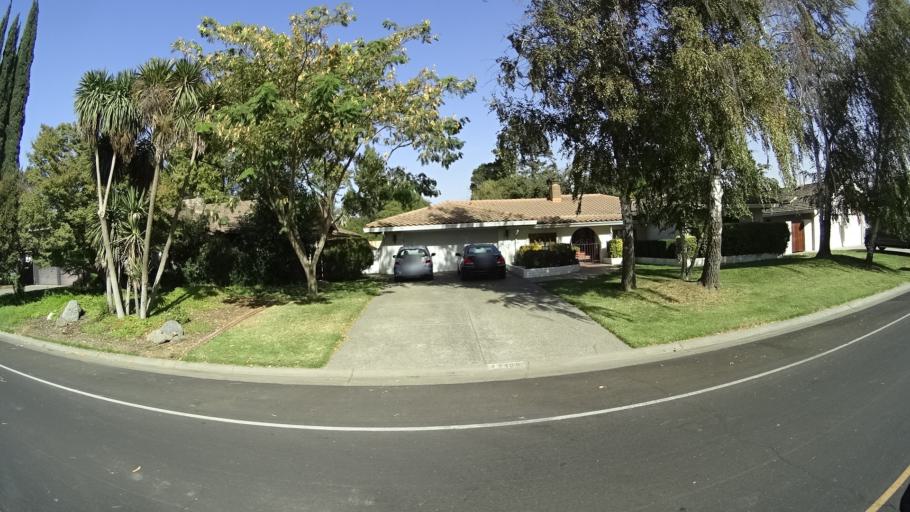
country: US
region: California
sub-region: Yolo County
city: Davis
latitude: 38.5477
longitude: -121.6859
